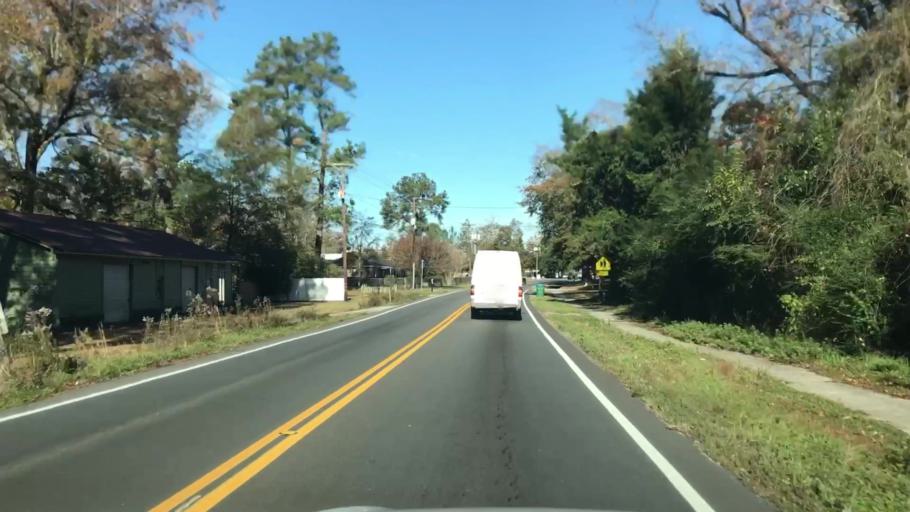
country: US
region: South Carolina
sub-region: Dorchester County
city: Summerville
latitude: 33.0056
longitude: -80.2350
